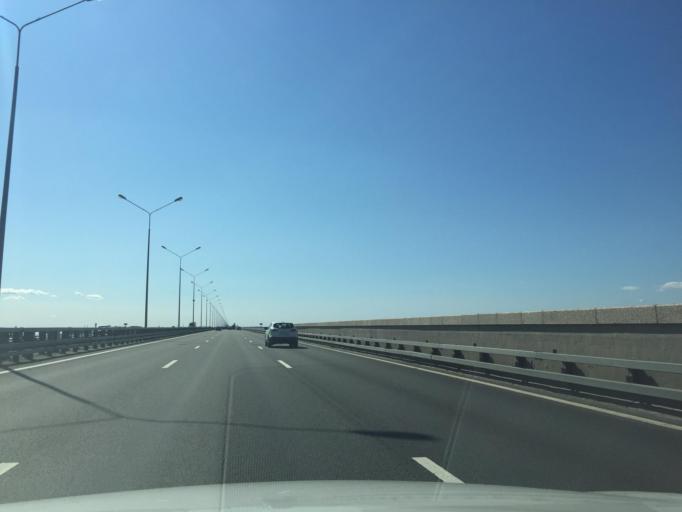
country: RU
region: Leningrad
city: Gorskaya
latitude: 60.0363
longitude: 29.9407
